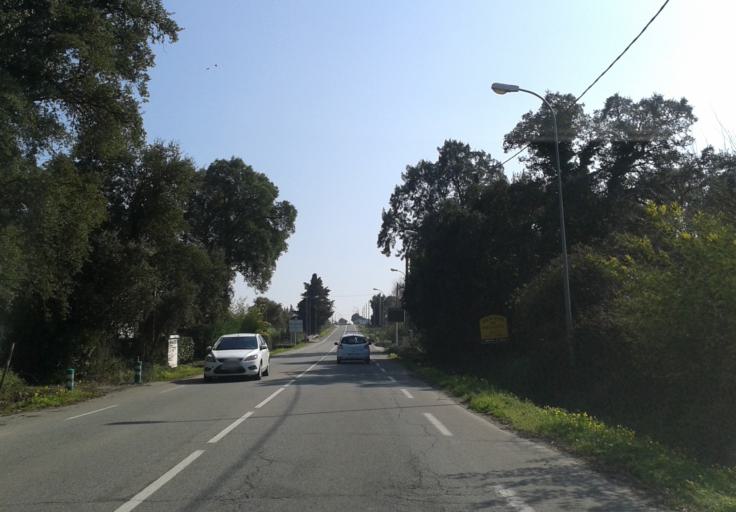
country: FR
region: Corsica
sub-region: Departement de la Haute-Corse
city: Cervione
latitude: 42.3243
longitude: 9.5389
